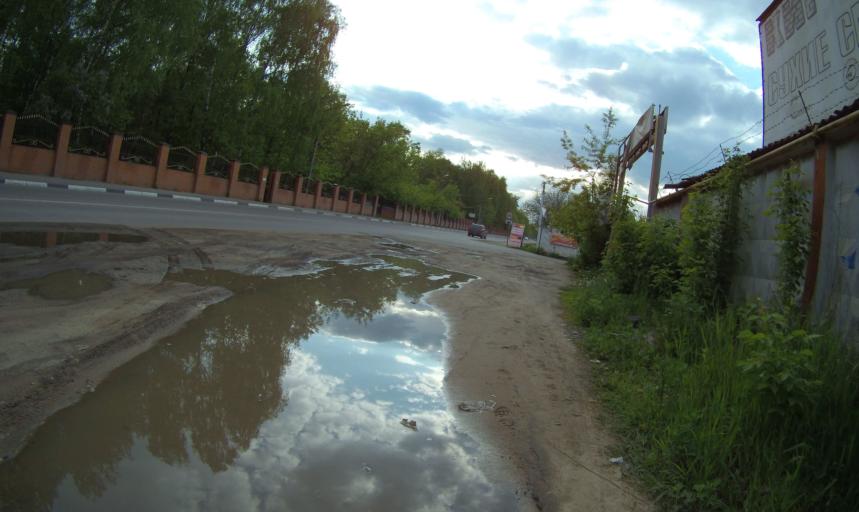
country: RU
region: Moskovskaya
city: Ramenskoye
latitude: 55.5692
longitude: 38.2562
